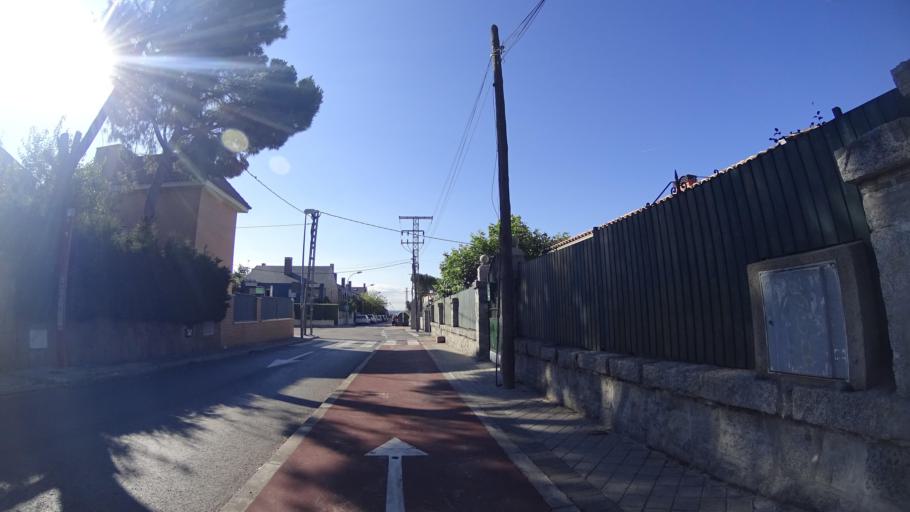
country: ES
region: Madrid
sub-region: Provincia de Madrid
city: Las Matas
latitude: 40.5520
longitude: -3.8904
